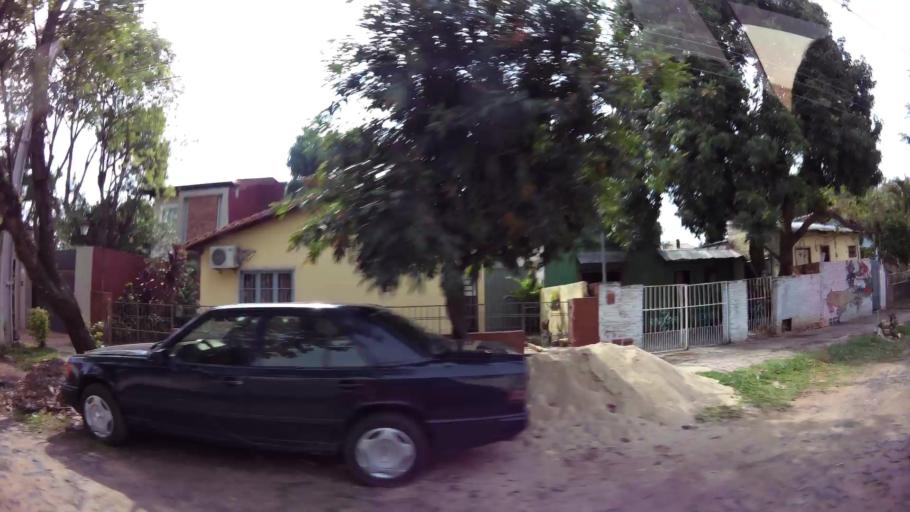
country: PY
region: Central
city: Fernando de la Mora
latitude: -25.3026
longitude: -57.5557
